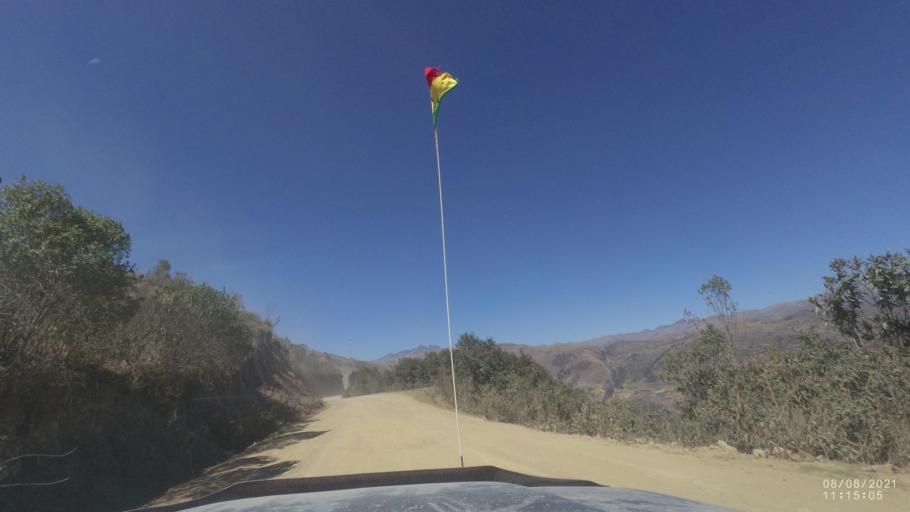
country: BO
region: Cochabamba
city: Colchani
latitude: -16.7739
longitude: -66.6674
